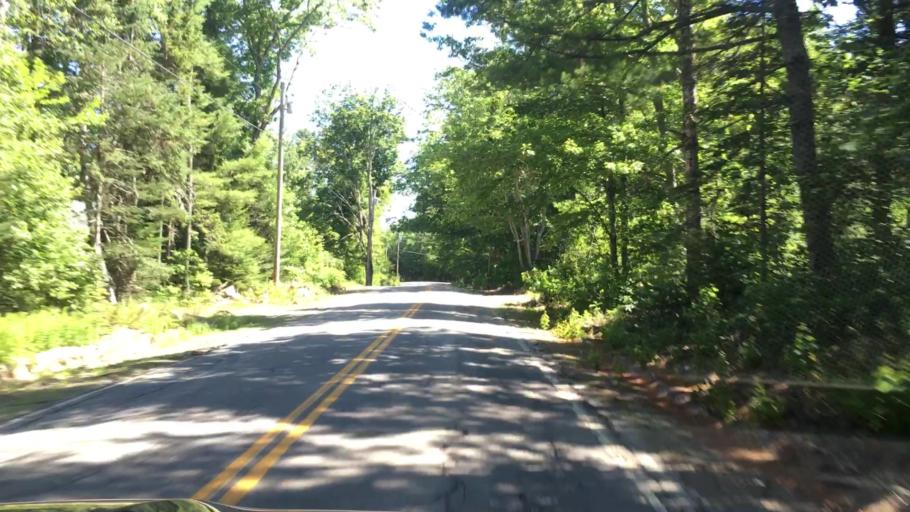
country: US
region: Maine
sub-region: Hancock County
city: Penobscot
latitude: 44.4387
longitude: -68.7098
